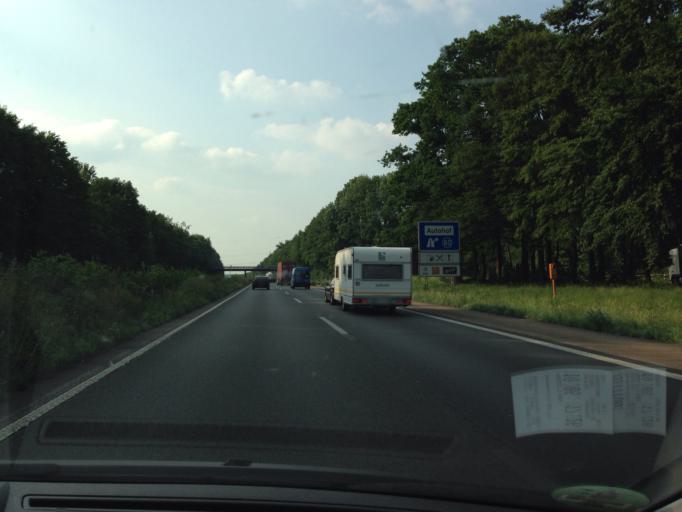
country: DE
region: North Rhine-Westphalia
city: Werne
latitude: 51.6752
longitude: 7.6799
